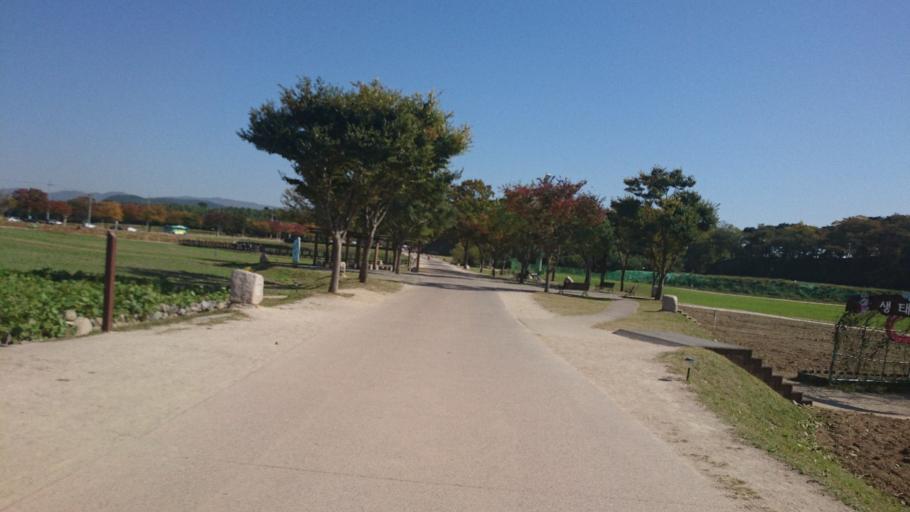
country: KR
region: Gyeongsangbuk-do
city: Kyonju
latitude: 35.8344
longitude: 129.2206
